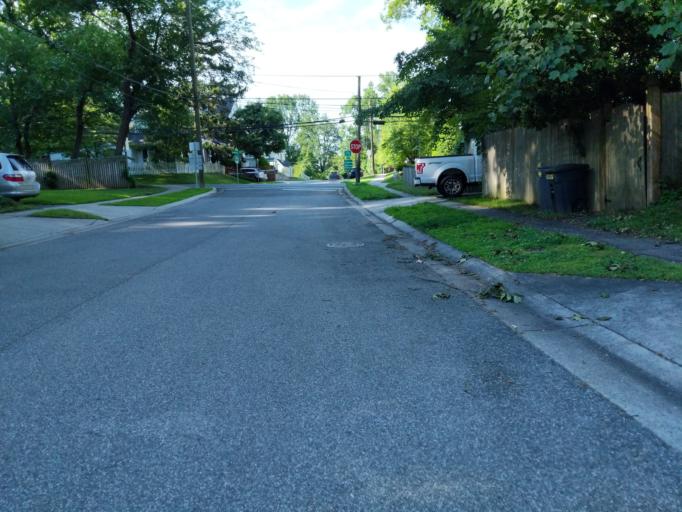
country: US
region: Maryland
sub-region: Montgomery County
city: Bethesda
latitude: 39.0007
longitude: -77.1123
